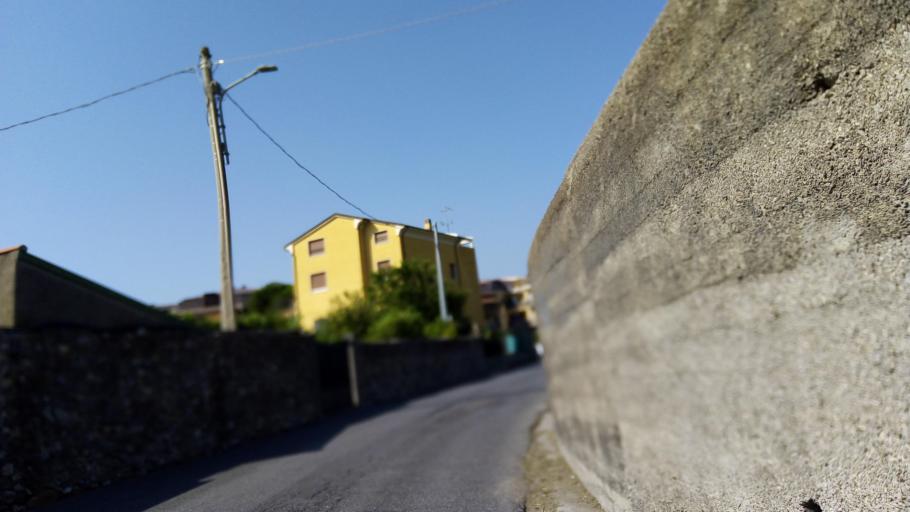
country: IT
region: Liguria
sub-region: Provincia di Savona
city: Borgio
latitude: 44.1584
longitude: 8.3012
